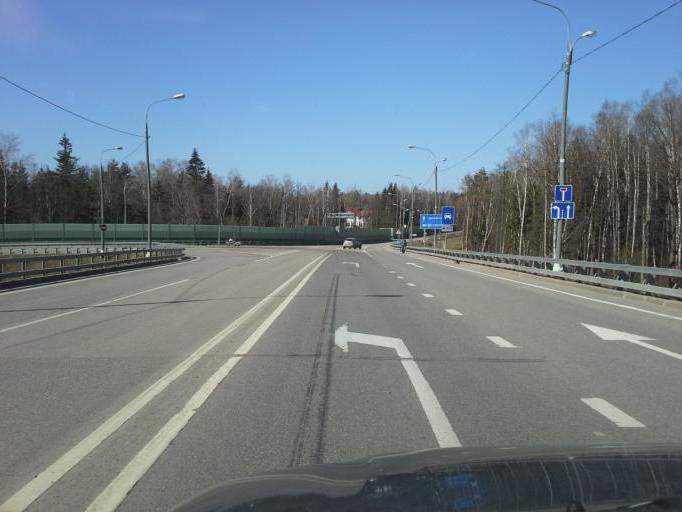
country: RU
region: Moskovskaya
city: Kokoshkino
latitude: 55.6247
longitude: 37.1528
